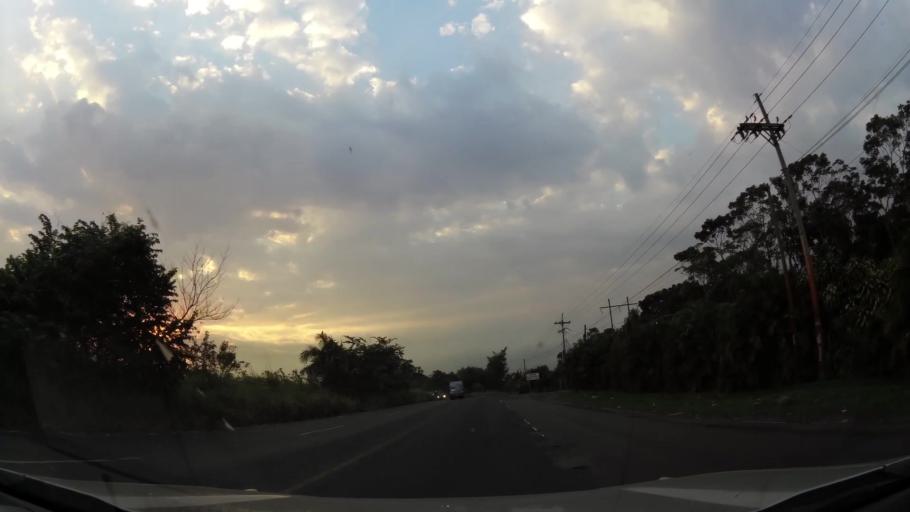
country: GT
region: Escuintla
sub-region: Municipio de La Democracia
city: La Democracia
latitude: 14.2749
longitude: -90.9130
